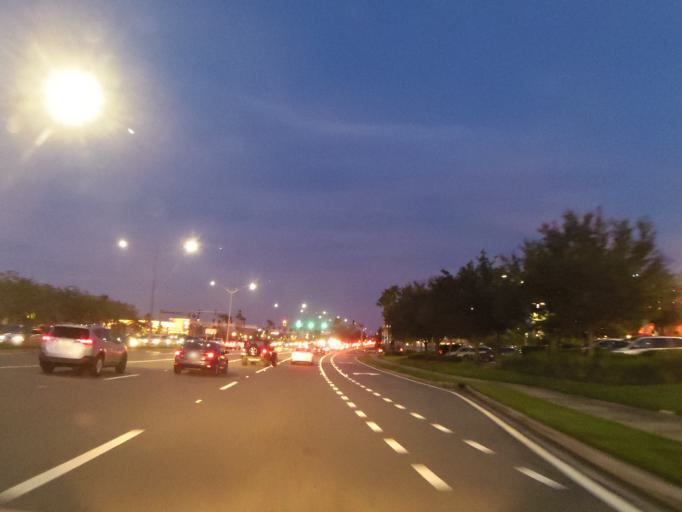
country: US
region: Florida
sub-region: Duval County
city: Jacksonville
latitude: 30.2546
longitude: -81.5356
